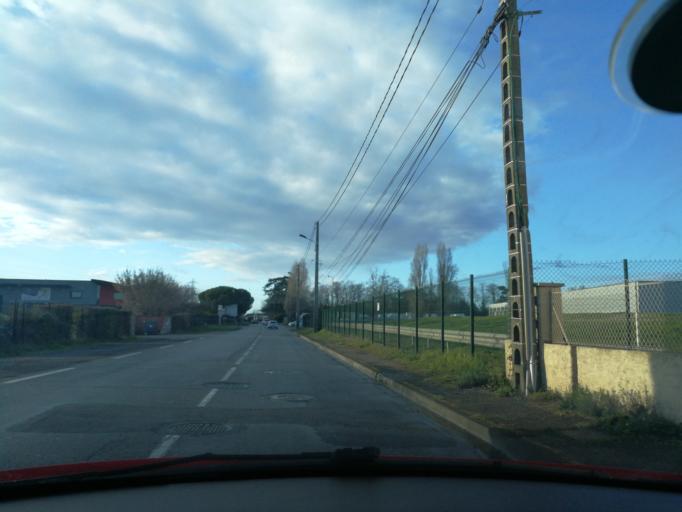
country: FR
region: Midi-Pyrenees
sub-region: Departement de la Haute-Garonne
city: Blagnac
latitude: 43.6399
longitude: 1.4185
